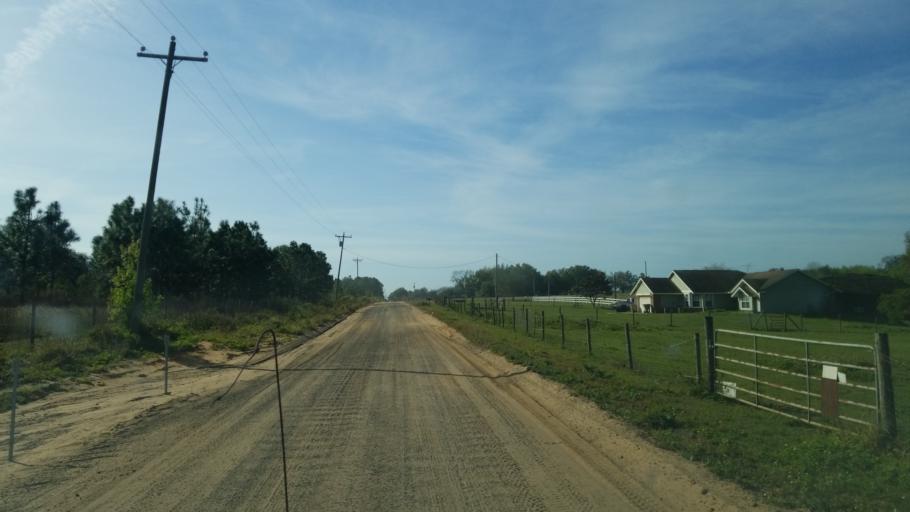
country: US
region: Florida
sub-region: Lake County
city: Clermont
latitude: 28.4551
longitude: -81.7570
